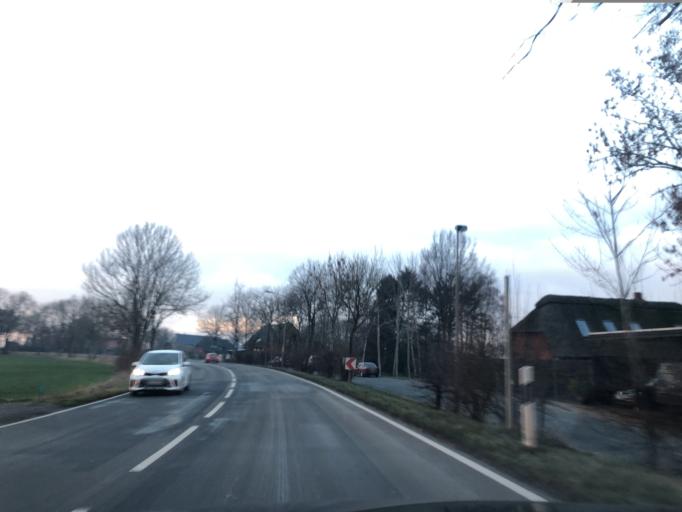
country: DE
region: Lower Saxony
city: Lemwerder
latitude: 53.1403
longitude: 8.5951
